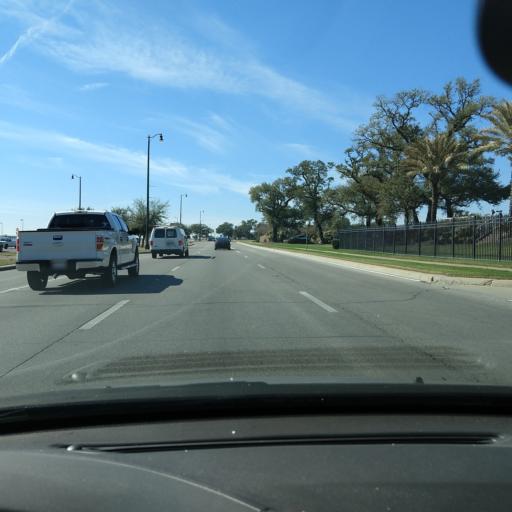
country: US
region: Mississippi
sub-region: Harrison County
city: Gulfport
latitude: 30.3625
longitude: -89.1026
